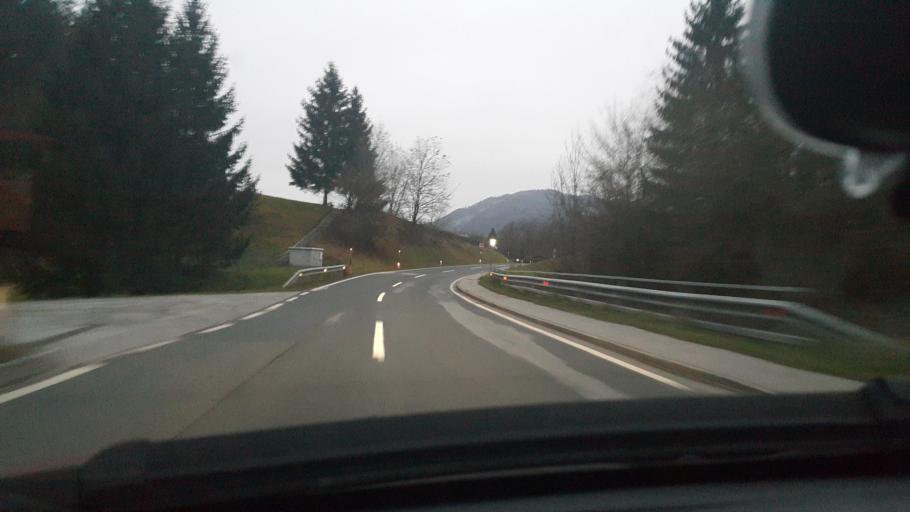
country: AT
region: Carinthia
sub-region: Politischer Bezirk Volkermarkt
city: Neuhaus
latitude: 46.6582
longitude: 14.8764
